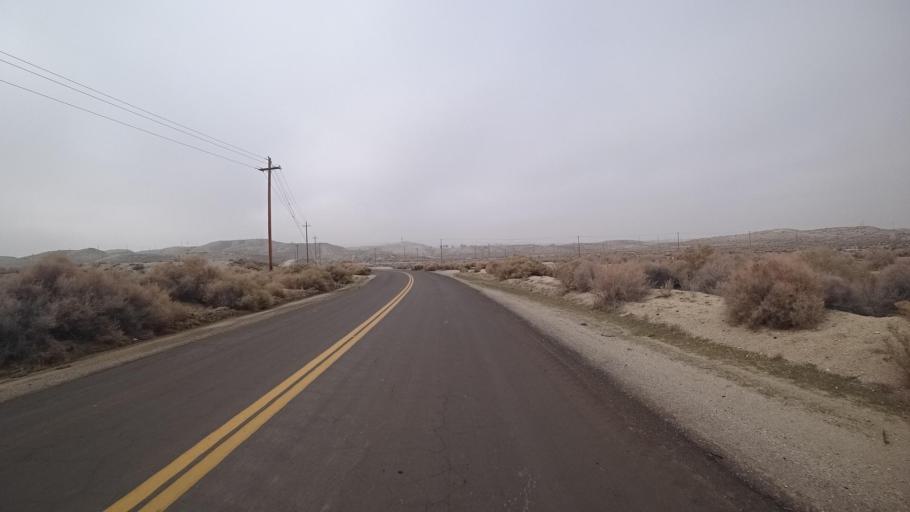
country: US
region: California
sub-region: Kern County
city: Maricopa
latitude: 35.0846
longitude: -119.3954
